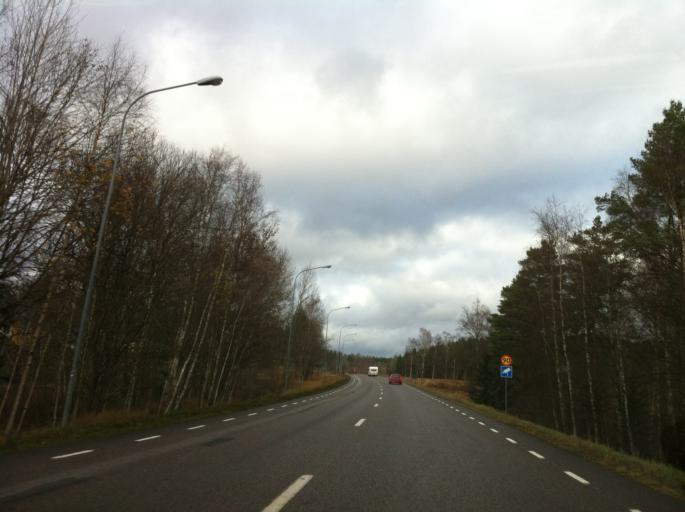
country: SE
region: Kalmar
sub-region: Vimmerby Kommun
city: Vimmerby
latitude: 57.5904
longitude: 15.8478
